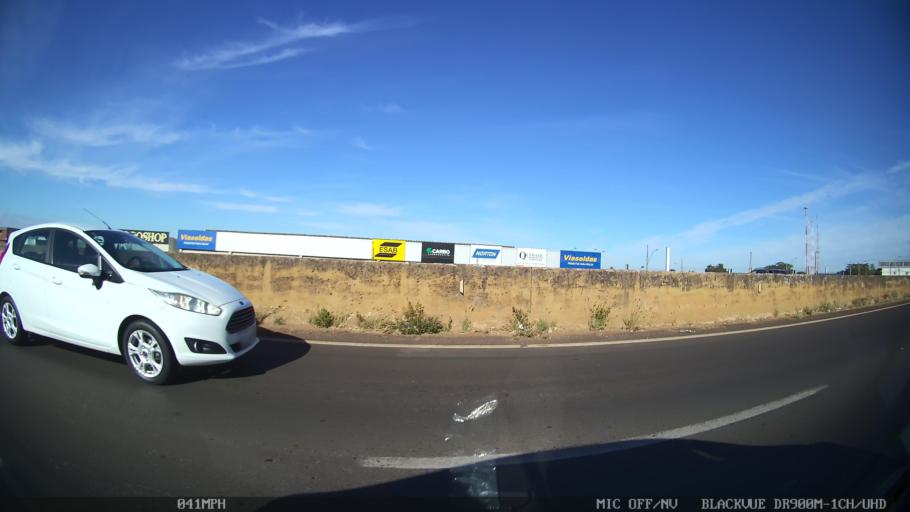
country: BR
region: Sao Paulo
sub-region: Sao Jose Do Rio Preto
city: Sao Jose do Rio Preto
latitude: -20.8268
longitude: -49.3591
